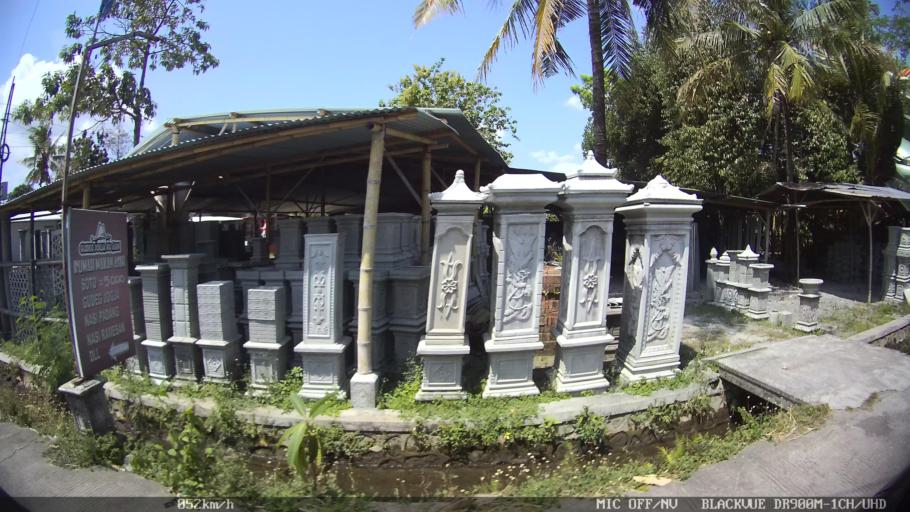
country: ID
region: Daerah Istimewa Yogyakarta
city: Pundong
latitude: -7.9356
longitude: 110.3740
